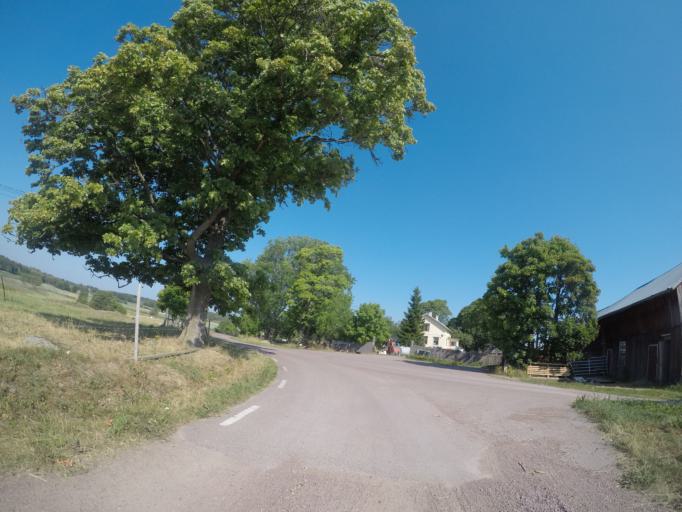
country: AX
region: Alands landsbygd
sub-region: Jomala
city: Jomala
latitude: 60.2041
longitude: 19.9753
